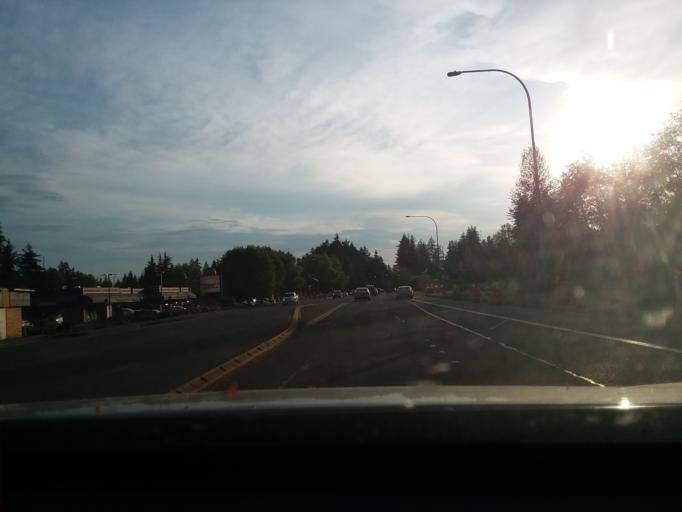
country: US
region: Washington
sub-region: Snohomish County
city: Mill Creek
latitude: 47.8783
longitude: -122.2088
